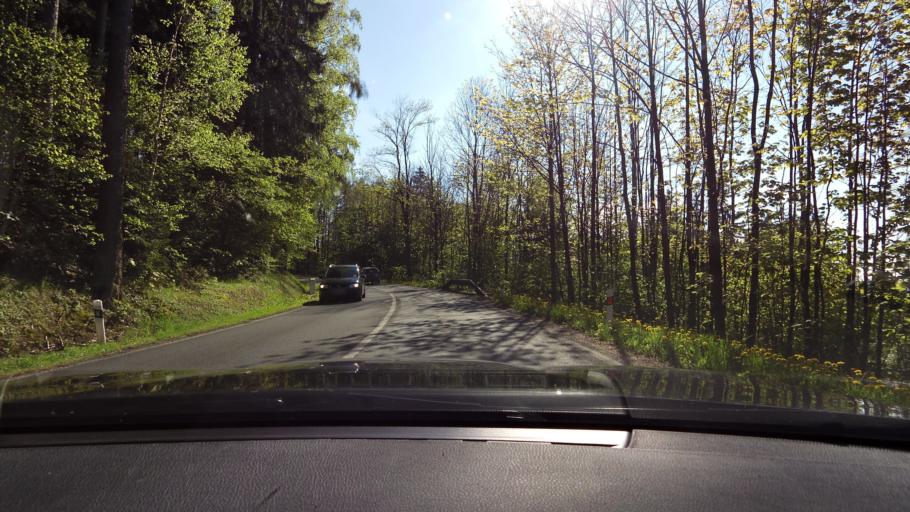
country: CZ
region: Plzensky
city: Strazov
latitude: 49.2752
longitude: 13.3025
